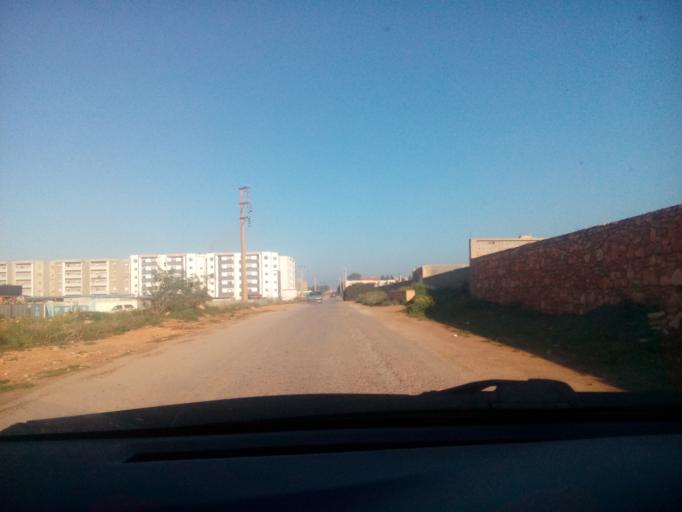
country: DZ
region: Oran
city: Bir el Djir
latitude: 35.7525
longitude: -0.5291
